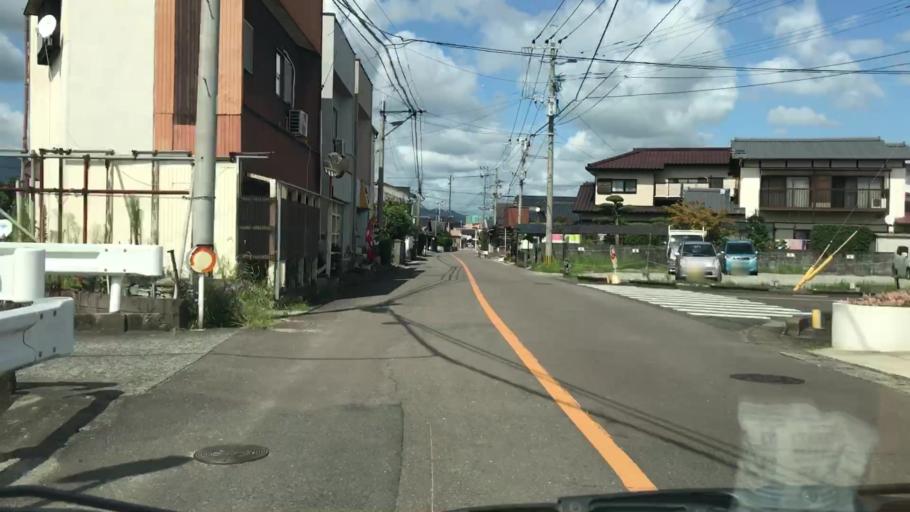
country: JP
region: Saga Prefecture
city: Saga-shi
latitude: 33.2444
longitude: 130.2027
